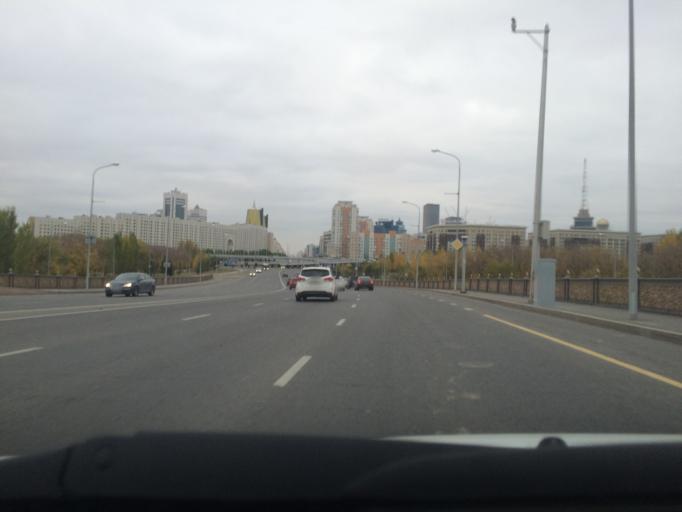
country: KZ
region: Astana Qalasy
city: Astana
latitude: 51.1365
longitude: 71.4420
